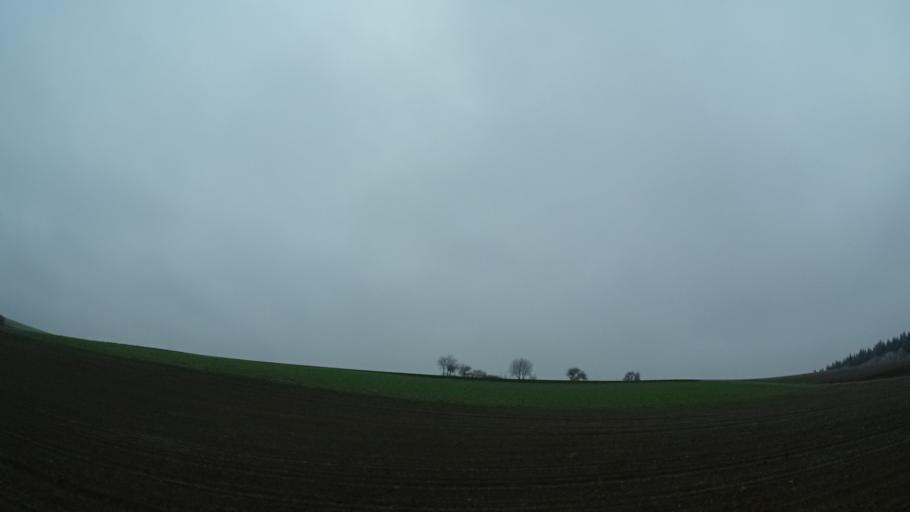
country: DE
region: Baden-Wuerttemberg
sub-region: Regierungsbezirk Stuttgart
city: Boxberg
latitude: 49.4941
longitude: 9.6352
